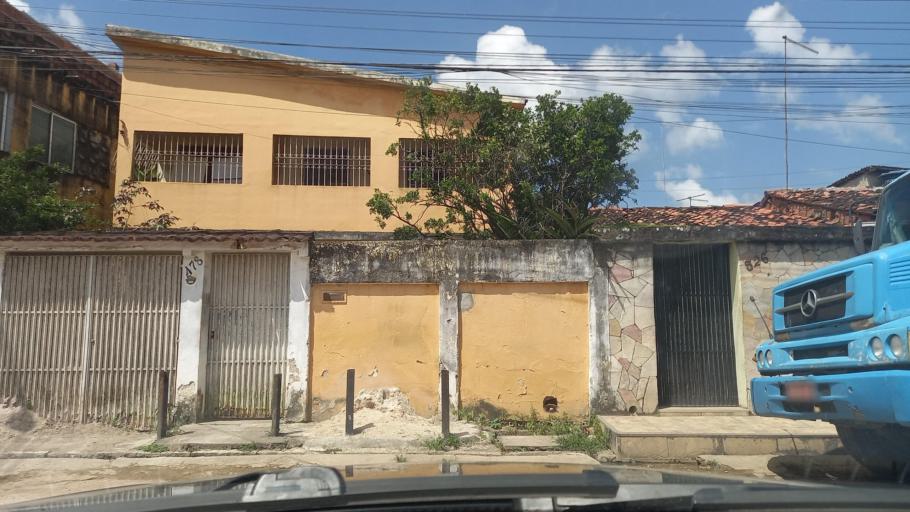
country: BR
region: Pernambuco
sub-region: Goiana
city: Goiana
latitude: -7.5649
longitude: -34.9939
